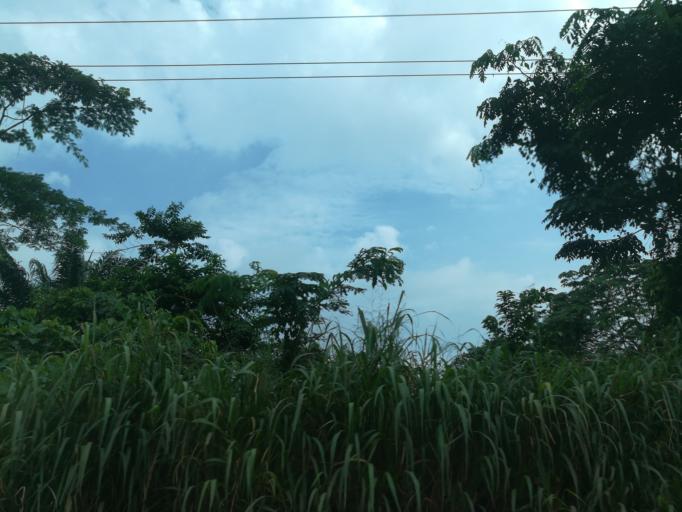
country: NG
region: Lagos
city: Ikorodu
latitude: 6.6640
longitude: 3.6013
